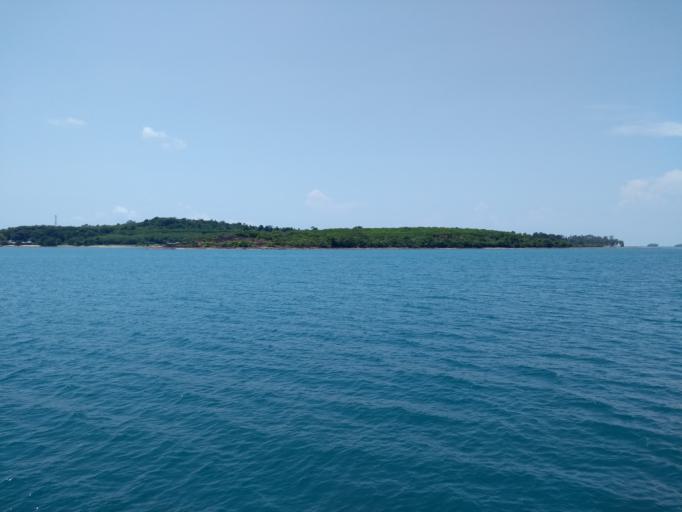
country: TH
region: Trat
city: Ko Kut
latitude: 11.8073
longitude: 102.5067
